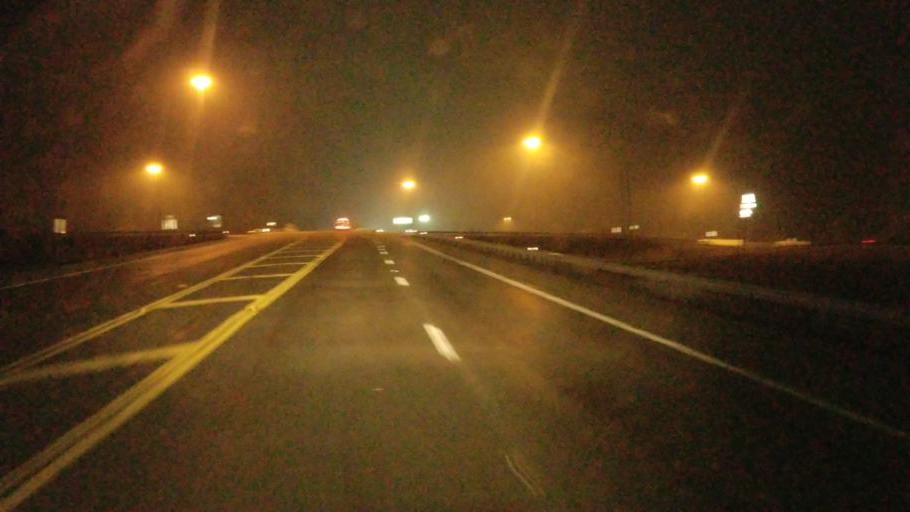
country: US
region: Ohio
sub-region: Preble County
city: Eaton
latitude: 39.8330
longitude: -84.6294
